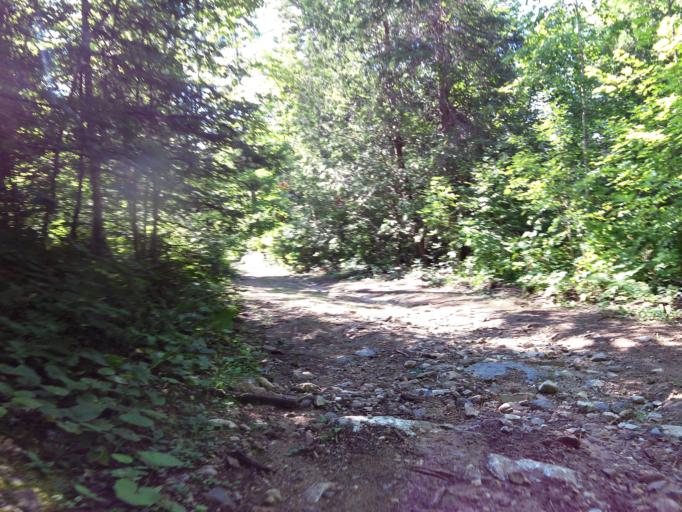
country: CA
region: Ontario
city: Renfrew
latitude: 45.1269
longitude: -76.7379
